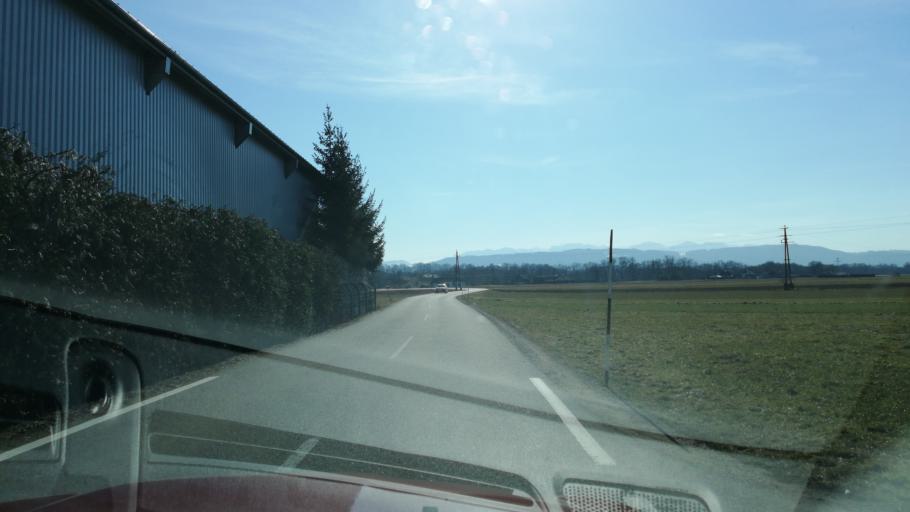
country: AT
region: Upper Austria
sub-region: Politischer Bezirk Vocklabruck
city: Redlham
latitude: 48.0197
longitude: 13.7419
